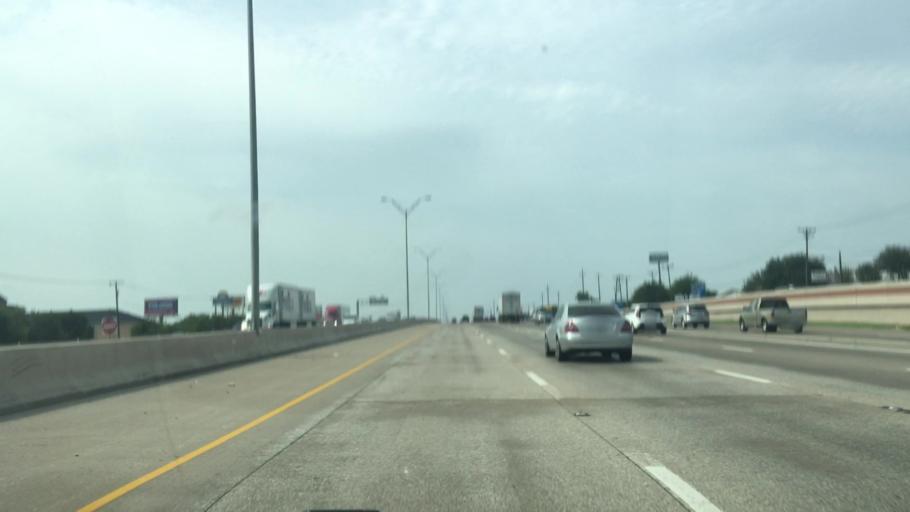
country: US
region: Texas
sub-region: Dallas County
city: DeSoto
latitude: 32.6151
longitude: -96.8230
